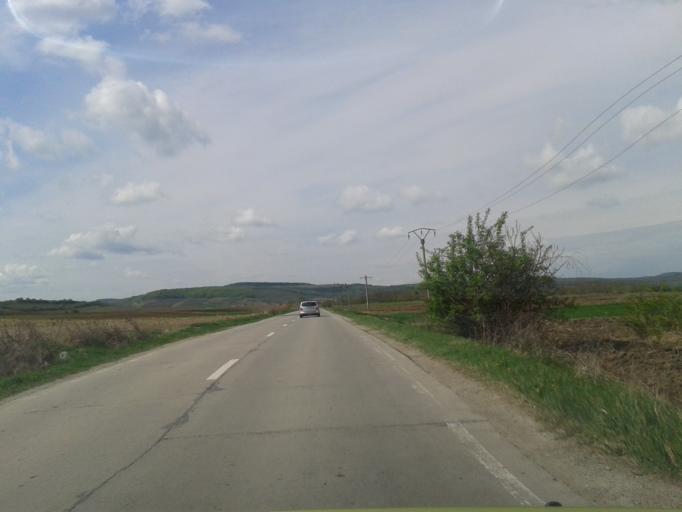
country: RO
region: Sibiu
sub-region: Comuna Micasasa
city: Micasasa
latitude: 46.0768
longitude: 24.1150
